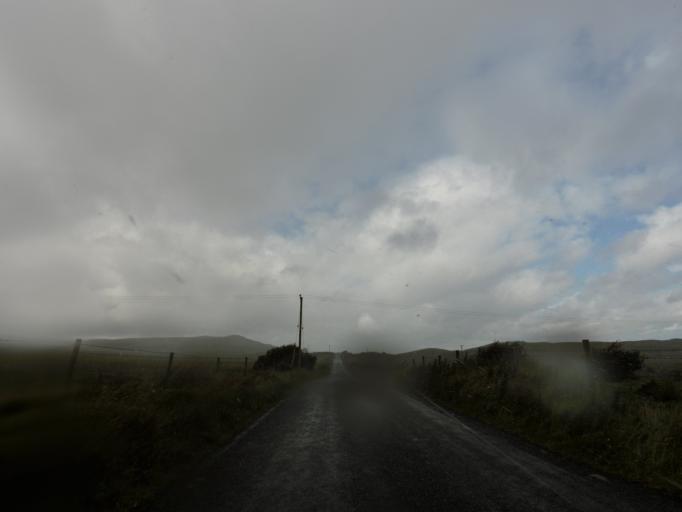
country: IE
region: Connaught
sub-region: County Galway
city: Oughterard
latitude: 53.4008
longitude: -9.3321
